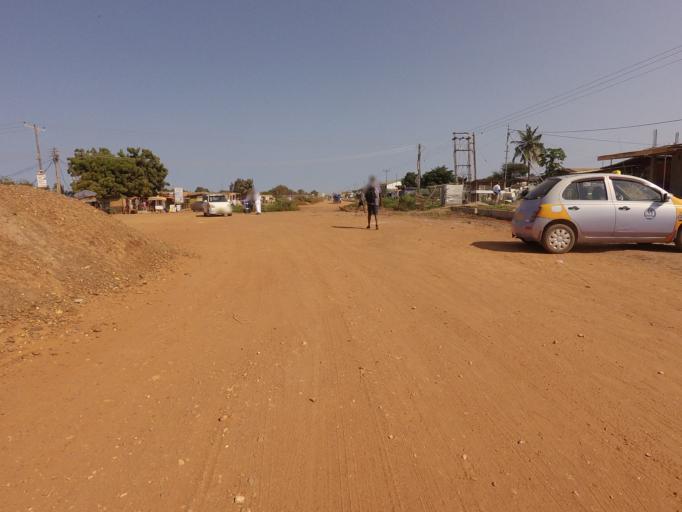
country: GH
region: Greater Accra
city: Teshi Old Town
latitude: 5.5890
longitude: -0.1156
